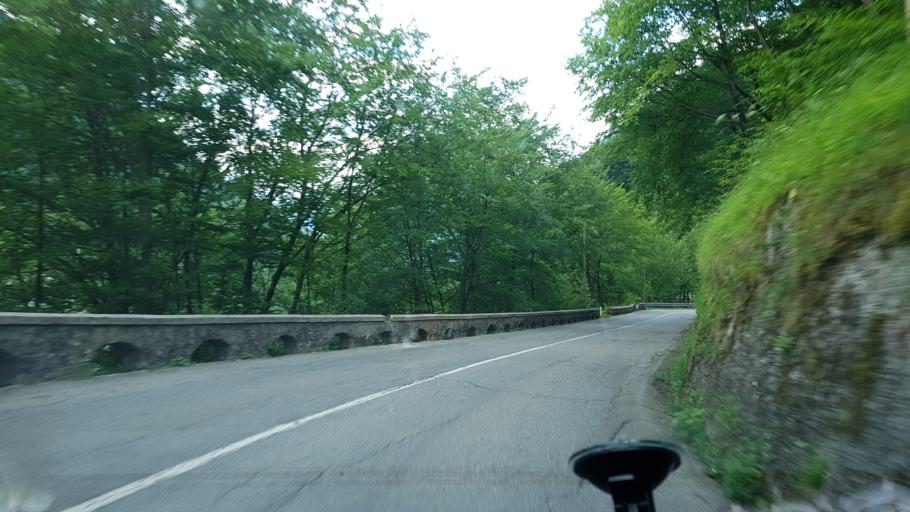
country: SI
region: Bovec
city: Bovec
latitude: 46.3078
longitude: 13.4654
